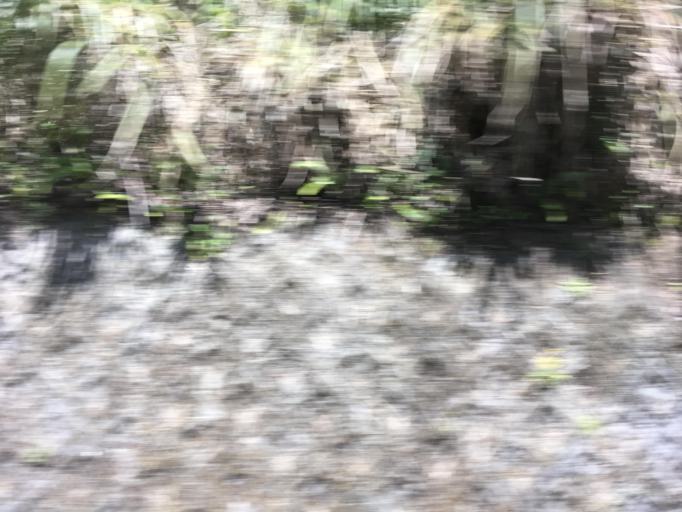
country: TW
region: Taiwan
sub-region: Yilan
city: Yilan
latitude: 24.5287
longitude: 121.5215
